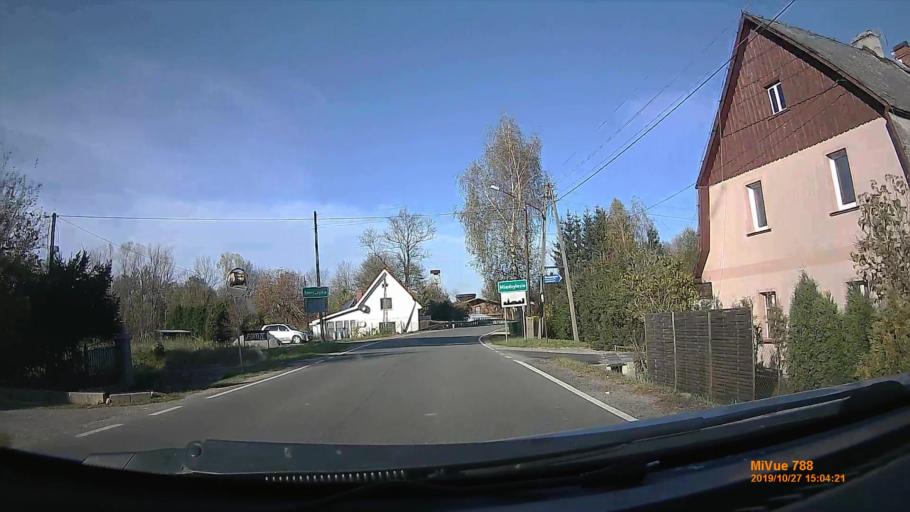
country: PL
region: Lower Silesian Voivodeship
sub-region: Powiat klodzki
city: Miedzylesie
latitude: 50.1398
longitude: 16.6628
